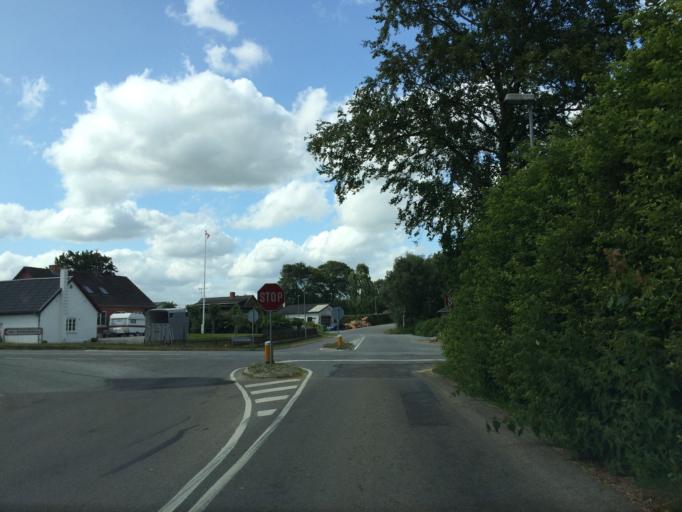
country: DK
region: Central Jutland
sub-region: Favrskov Kommune
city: Hammel
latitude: 56.2141
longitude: 9.7517
